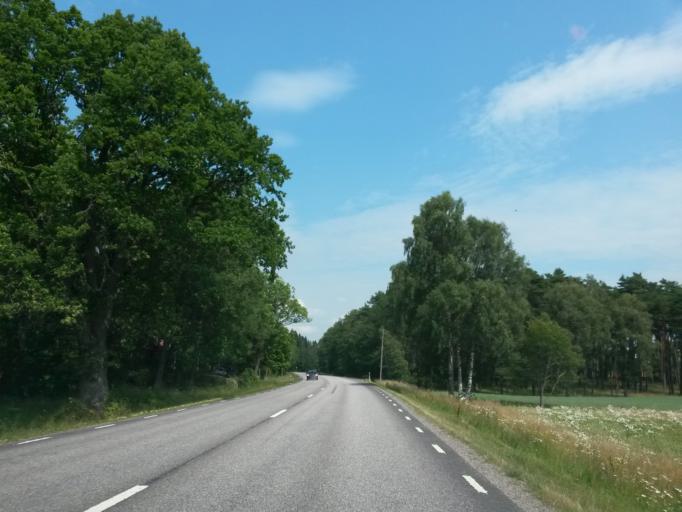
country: SE
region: Vaestra Goetaland
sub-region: Grastorps Kommun
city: Graestorp
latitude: 58.3681
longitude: 12.7189
